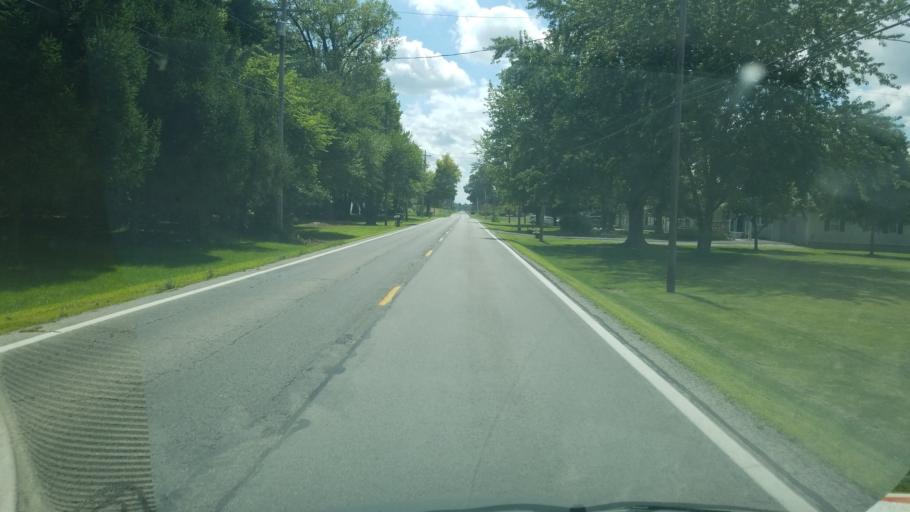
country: US
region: Ohio
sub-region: Henry County
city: Liberty Center
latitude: 41.4698
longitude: -84.0087
